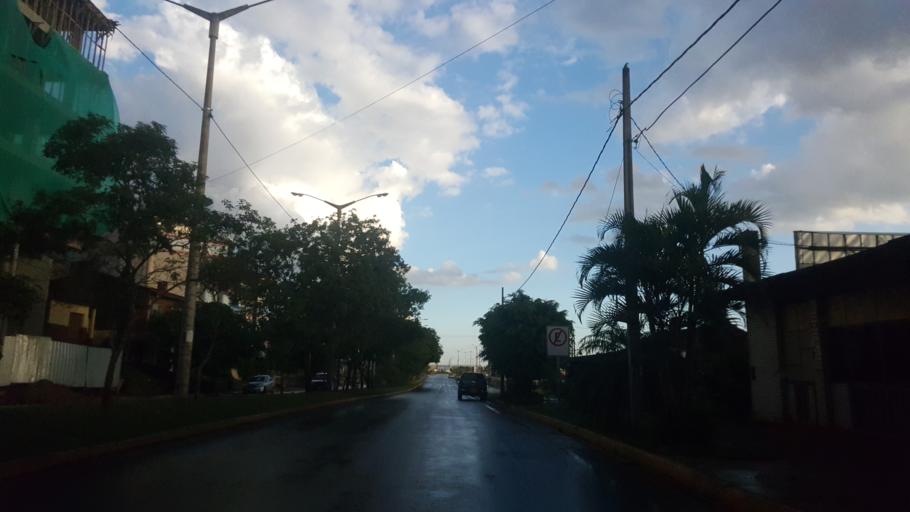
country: PY
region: Itapua
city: Encarnacion
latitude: -27.3334
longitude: -55.8725
